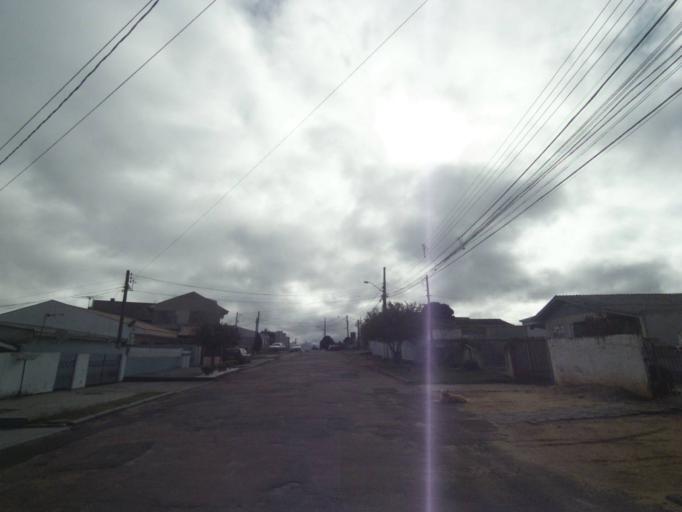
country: BR
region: Parana
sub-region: Sao Jose Dos Pinhais
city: Sao Jose dos Pinhais
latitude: -25.5214
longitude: -49.3002
